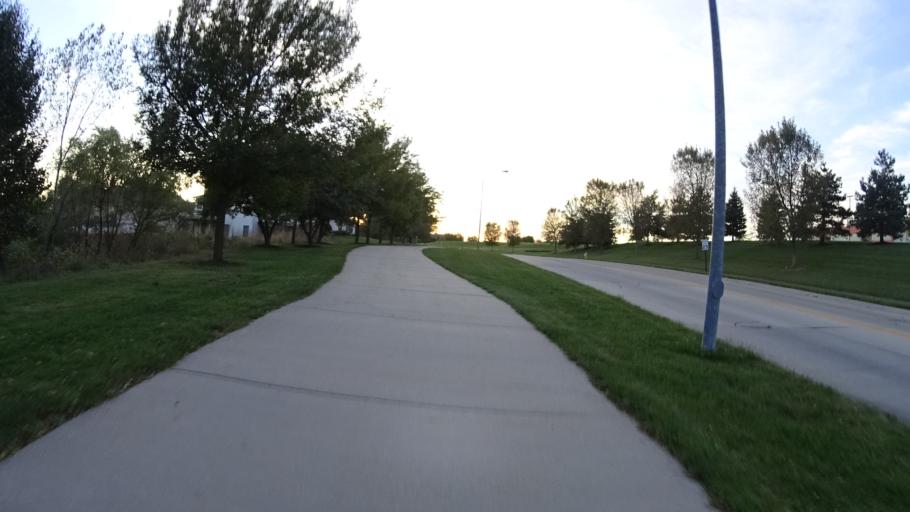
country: US
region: Nebraska
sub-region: Sarpy County
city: Papillion
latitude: 41.1382
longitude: -95.9816
